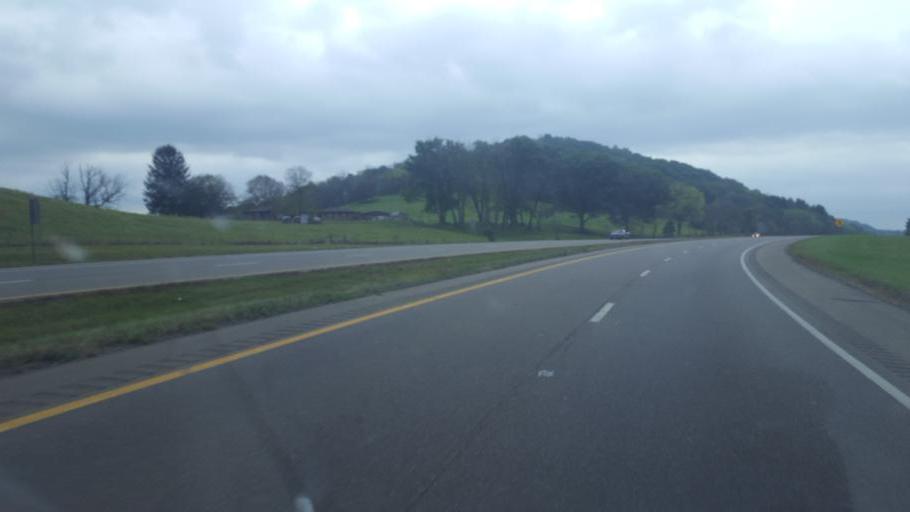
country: US
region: Ohio
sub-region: Tuscarawas County
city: New Philadelphia
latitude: 40.4557
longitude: -81.3991
